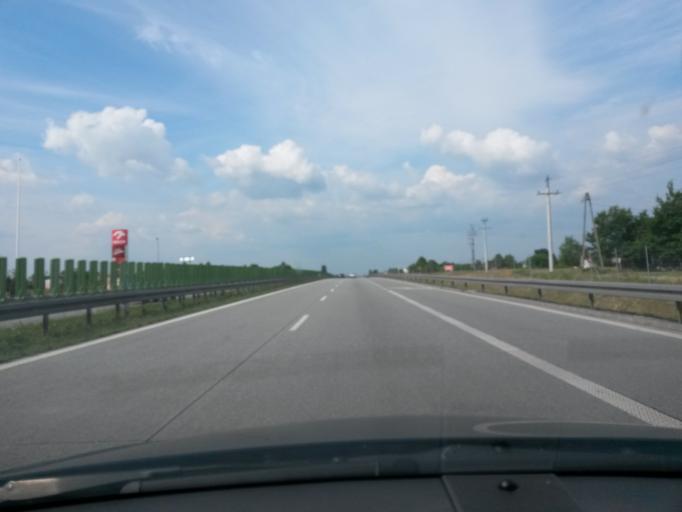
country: PL
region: Lodz Voivodeship
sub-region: Powiat rawski
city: Rawa Mazowiecka
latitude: 51.7355
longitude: 20.2317
